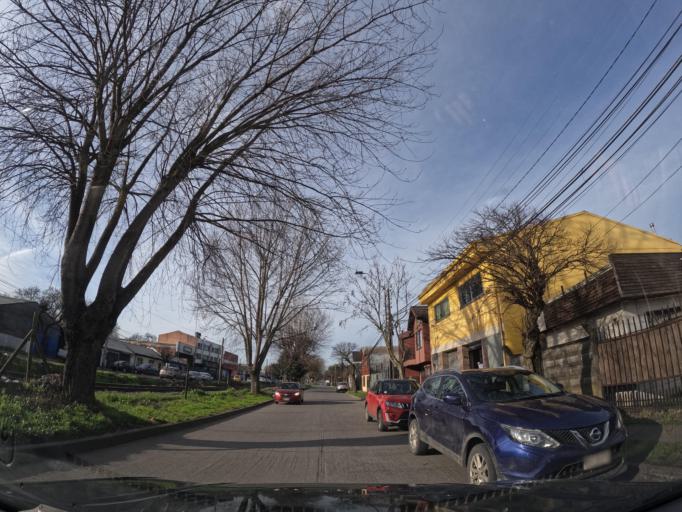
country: CL
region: Biobio
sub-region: Provincia de Concepcion
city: Concepcion
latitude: -36.8145
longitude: -73.0540
